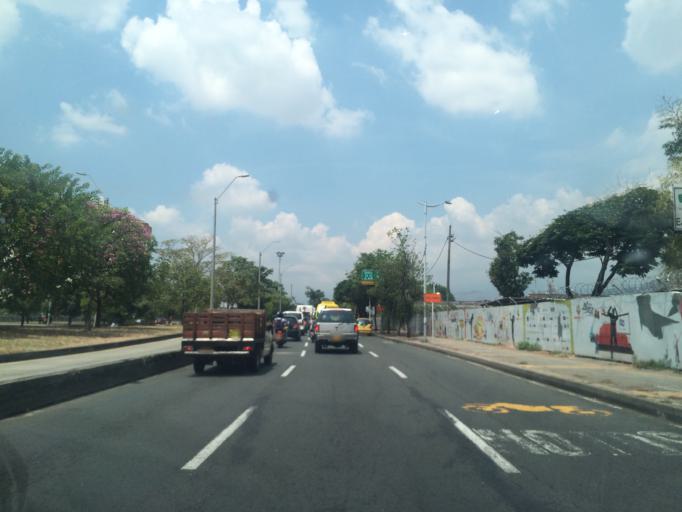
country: CO
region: Valle del Cauca
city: Cali
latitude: 3.4778
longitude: -76.5030
